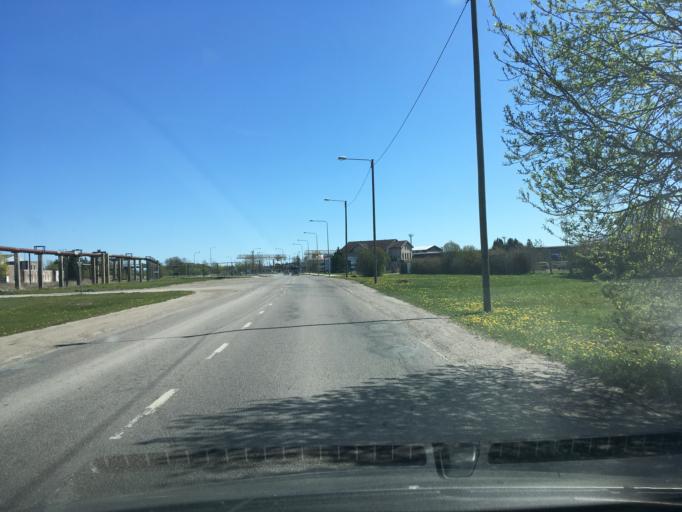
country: EE
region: Harju
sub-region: Joelaehtme vald
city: Loo
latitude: 59.4535
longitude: 24.9628
